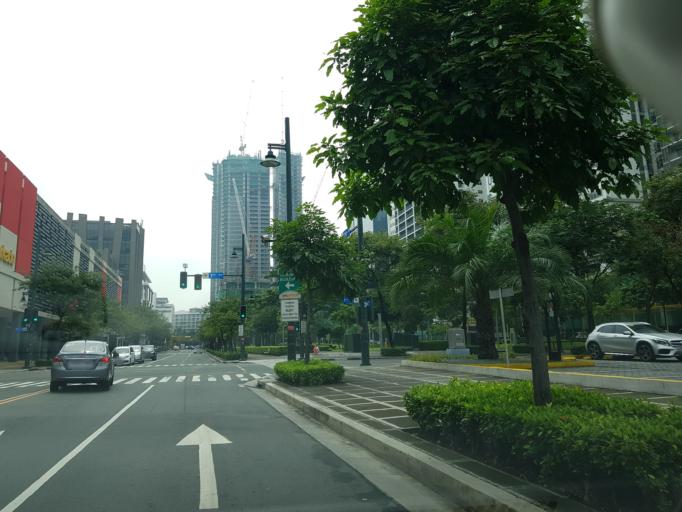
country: PH
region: Metro Manila
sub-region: Makati City
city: Makati City
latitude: 14.5501
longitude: 121.0488
